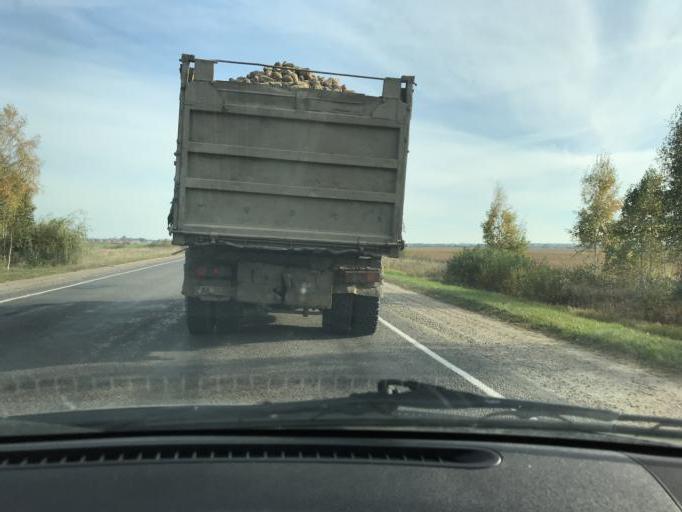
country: BY
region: Brest
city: Asnyezhytsy
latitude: 52.2117
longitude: 26.0460
